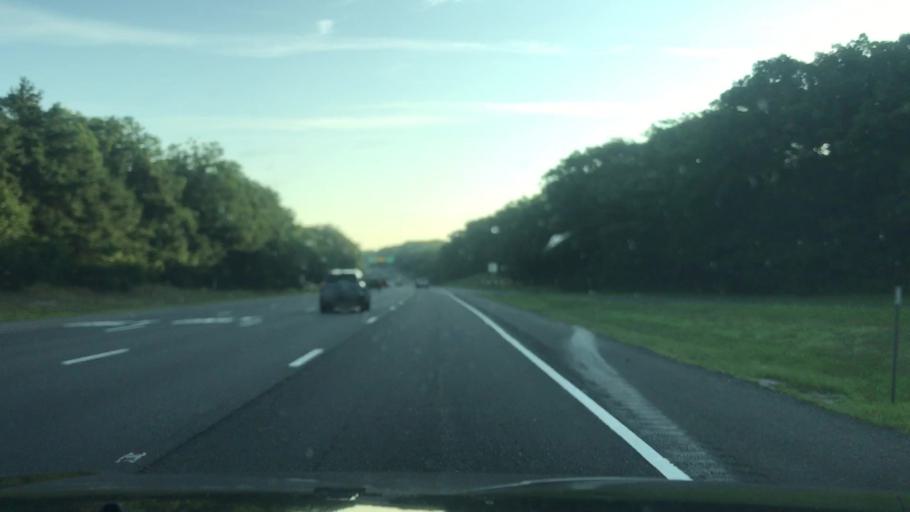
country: US
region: New Jersey
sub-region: Monmouth County
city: Shark River Hills
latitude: 40.2409
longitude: -74.0860
